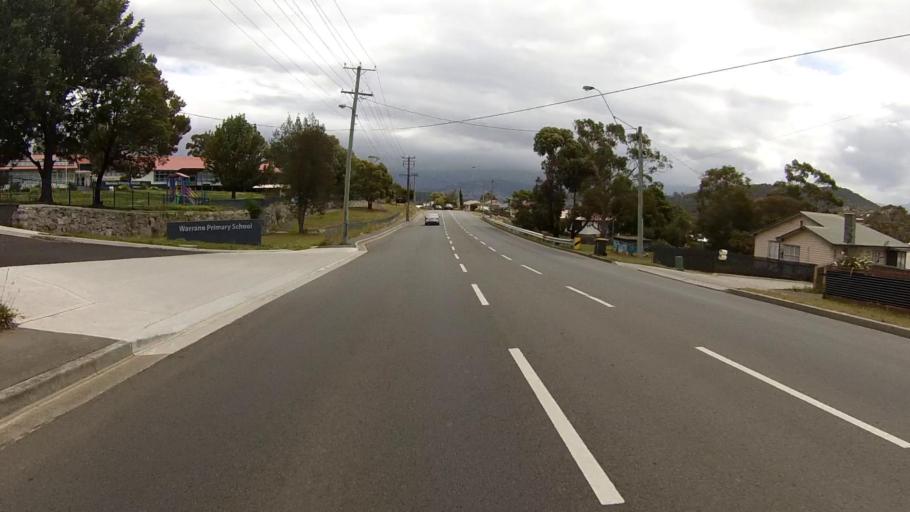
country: AU
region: Tasmania
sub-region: Clarence
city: Warrane
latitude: -42.8598
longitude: 147.3826
